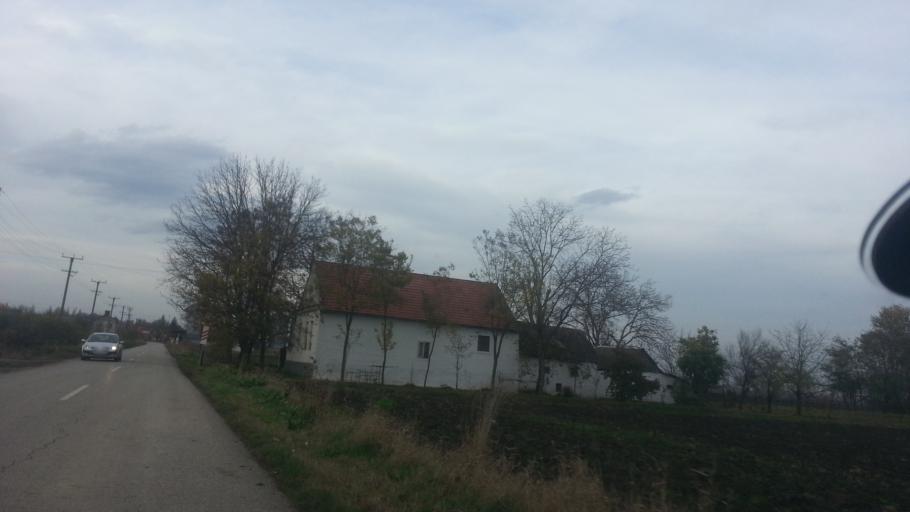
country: RS
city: Putinci
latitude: 44.9784
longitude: 19.9698
